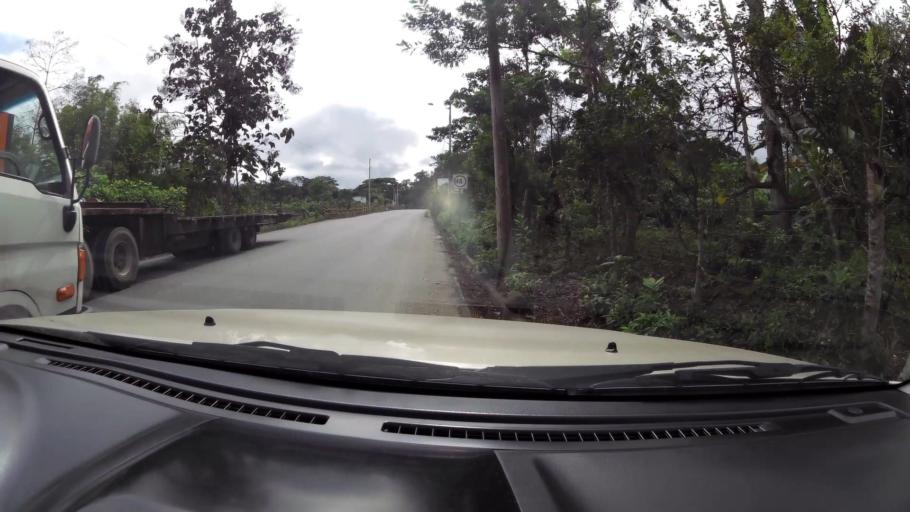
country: EC
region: El Oro
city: Pasaje
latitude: -3.3204
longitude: -79.6734
